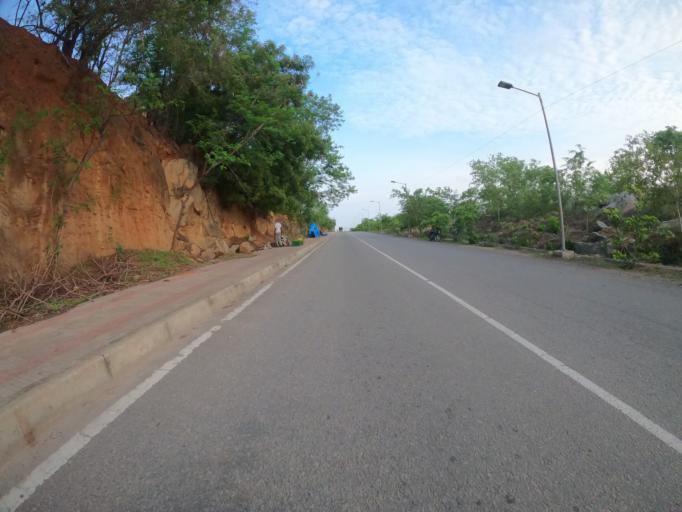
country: IN
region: Telangana
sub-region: Hyderabad
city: Hyderabad
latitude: 17.3538
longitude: 78.3585
